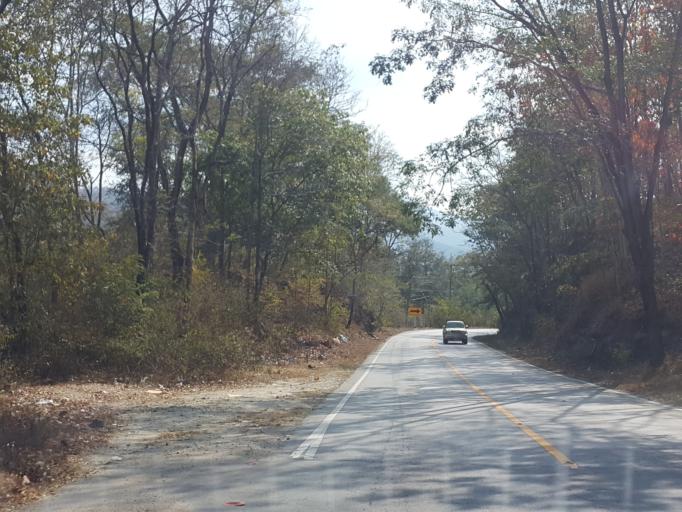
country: TH
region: Chiang Mai
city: Hot
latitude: 18.2170
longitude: 98.4453
